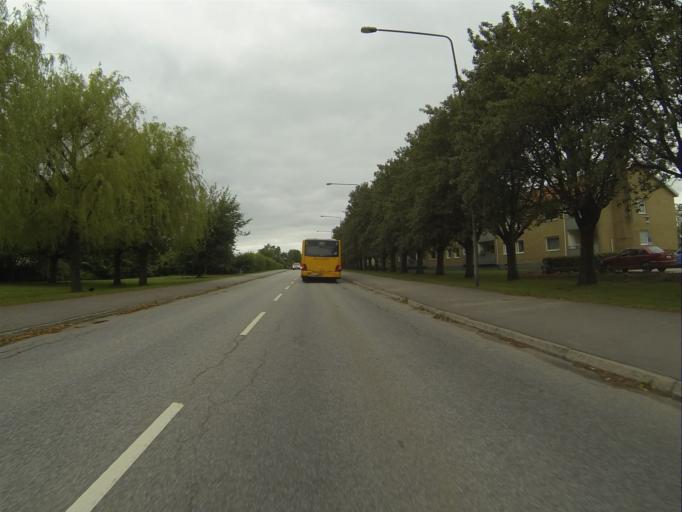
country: SE
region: Skane
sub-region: Staffanstorps Kommun
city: Staffanstorp
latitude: 55.6460
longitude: 13.2074
